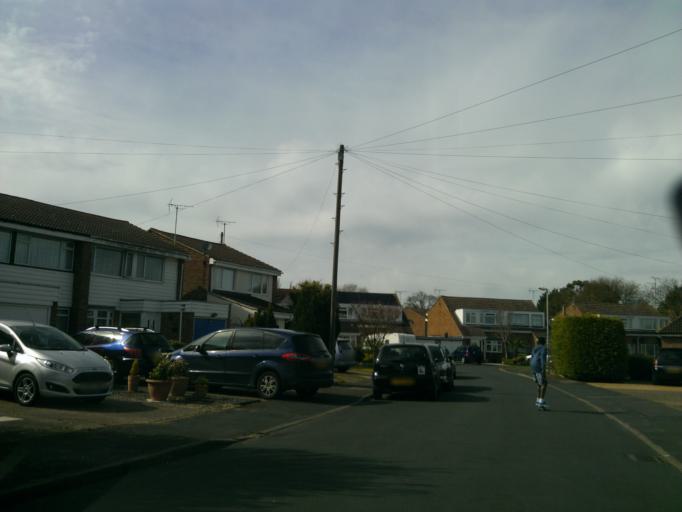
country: GB
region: England
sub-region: Essex
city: Witham
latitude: 51.8472
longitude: 0.6298
